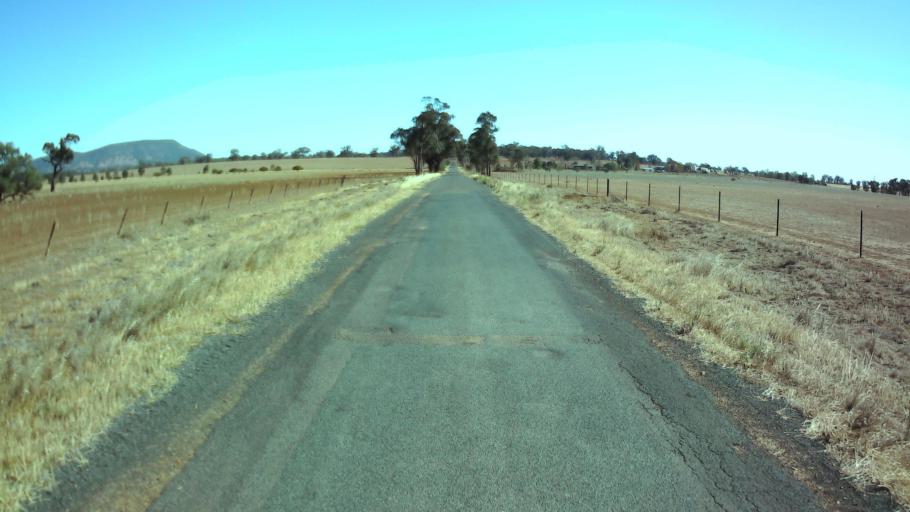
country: AU
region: New South Wales
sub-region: Weddin
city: Grenfell
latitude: -33.7975
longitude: 147.9563
